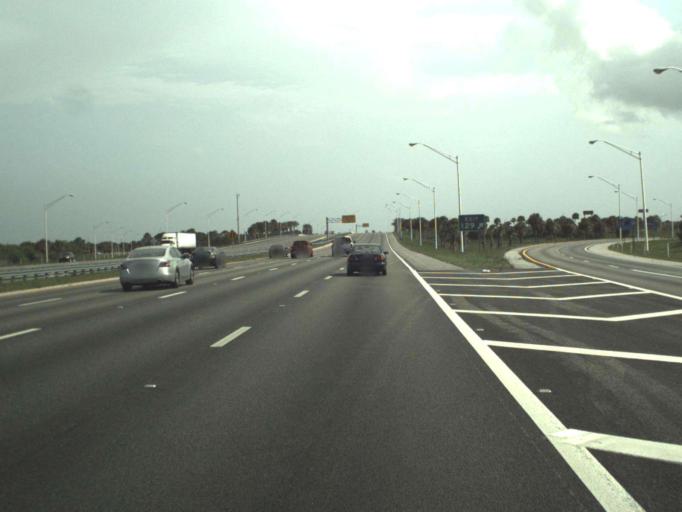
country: US
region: Florida
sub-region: Saint Lucie County
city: Fort Pierce South
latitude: 27.4216
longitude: -80.3886
